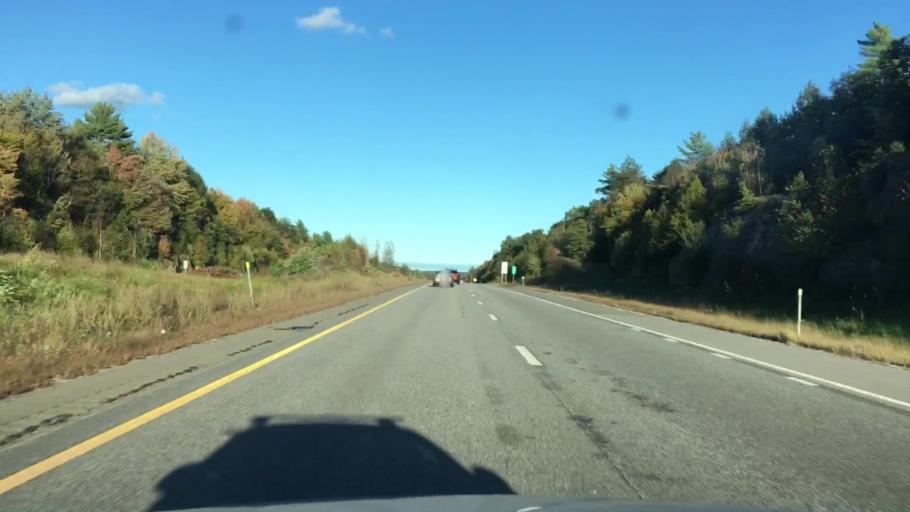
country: US
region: New Hampshire
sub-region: Rockingham County
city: Raymond
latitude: 43.0255
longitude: -71.1868
